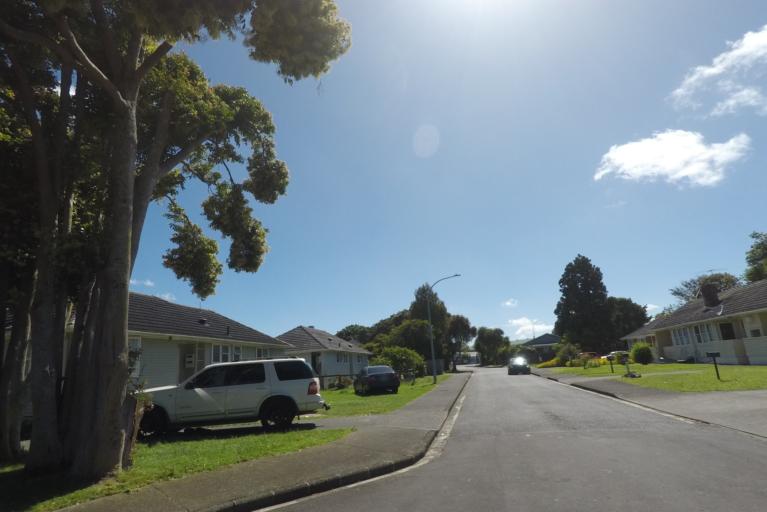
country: NZ
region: Auckland
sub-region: Auckland
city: Rosebank
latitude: -36.8907
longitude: 174.6861
